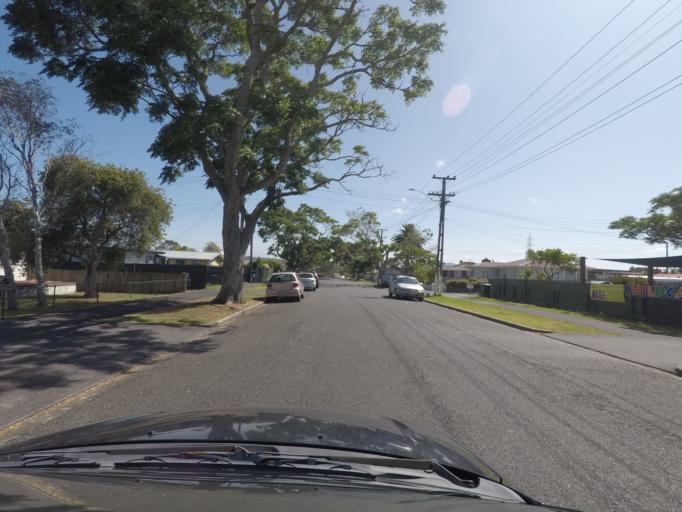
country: NZ
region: Auckland
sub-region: Auckland
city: Rosebank
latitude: -36.8961
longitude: 174.6828
